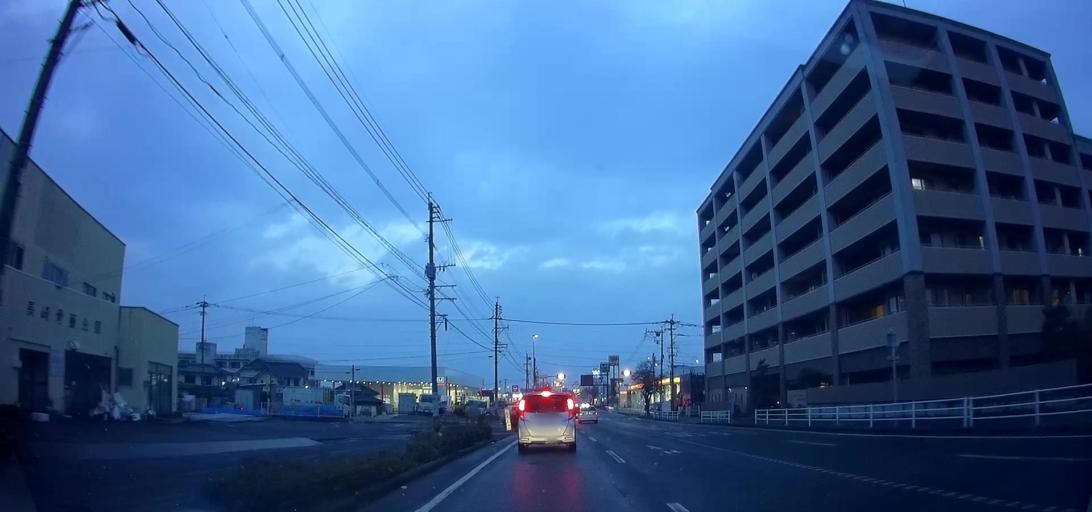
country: JP
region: Nagasaki
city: Omura
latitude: 32.9096
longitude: 129.9538
